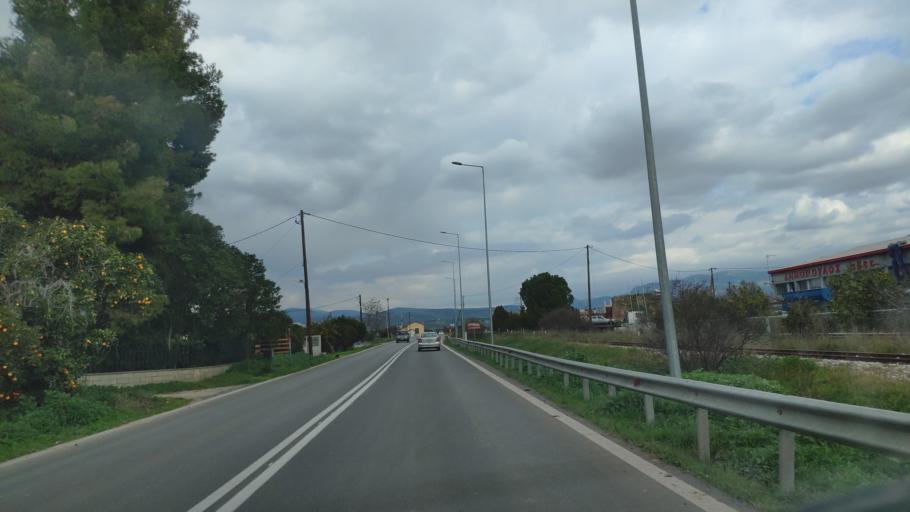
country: GR
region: Peloponnese
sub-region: Nomos Argolidos
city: Koutsopodi
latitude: 37.6822
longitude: 22.7191
